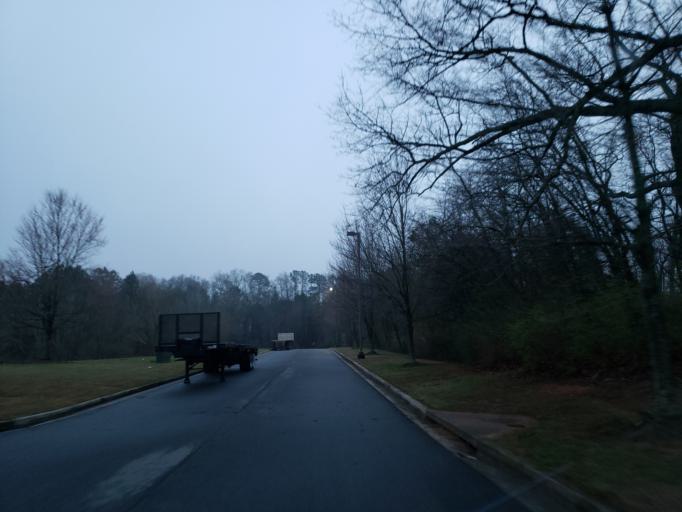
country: US
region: Georgia
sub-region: Cobb County
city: Marietta
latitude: 33.9736
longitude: -84.5591
